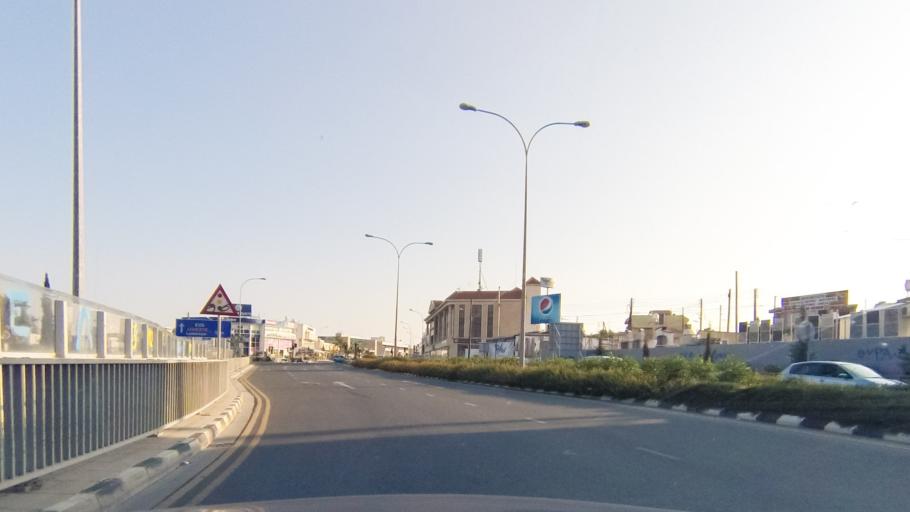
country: CY
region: Limassol
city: Mouttagiaka
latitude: 34.7079
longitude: 33.0870
